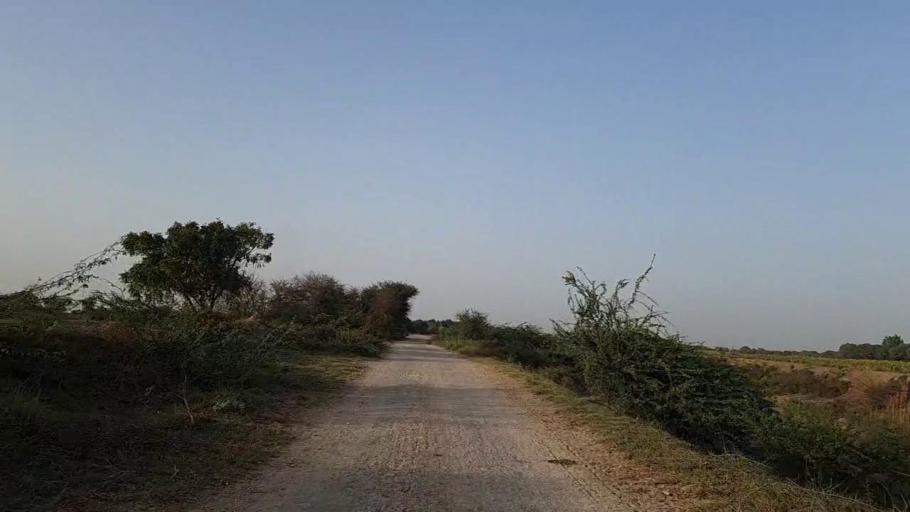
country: PK
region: Sindh
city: Jati
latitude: 24.4130
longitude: 68.1863
